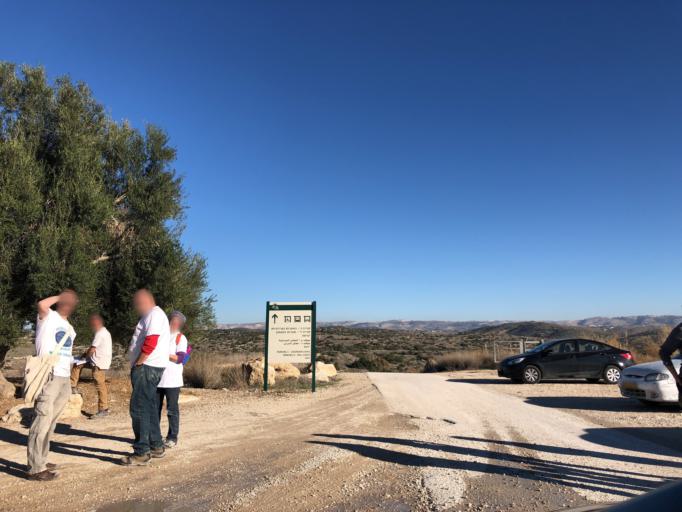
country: PS
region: West Bank
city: Idhna
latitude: 31.5920
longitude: 34.9001
